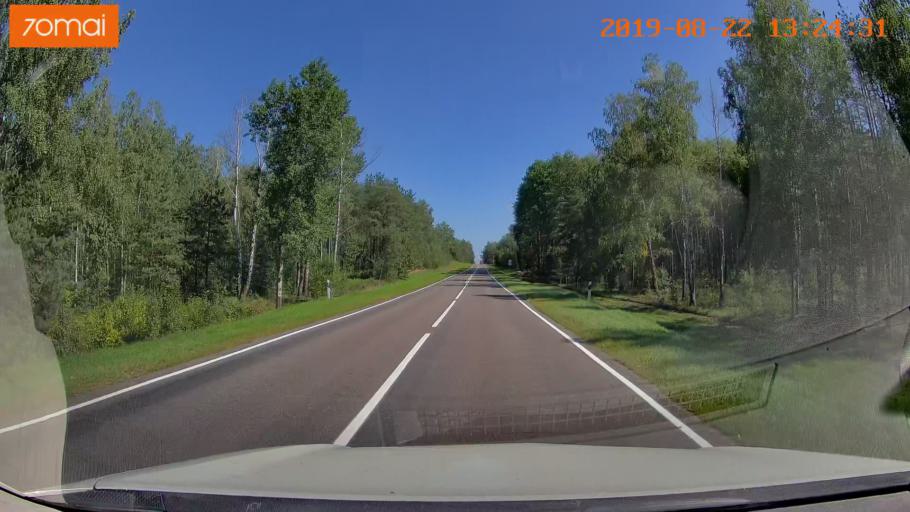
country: BY
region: Minsk
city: Urechcha
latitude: 53.2111
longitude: 28.0234
